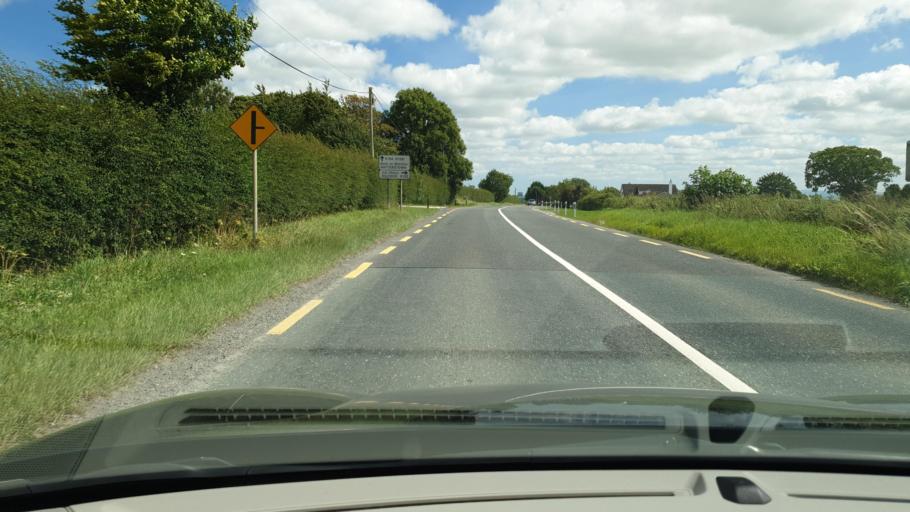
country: IE
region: Leinster
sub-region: An Mhi
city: Dunshaughlin
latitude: 53.5034
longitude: -6.5992
